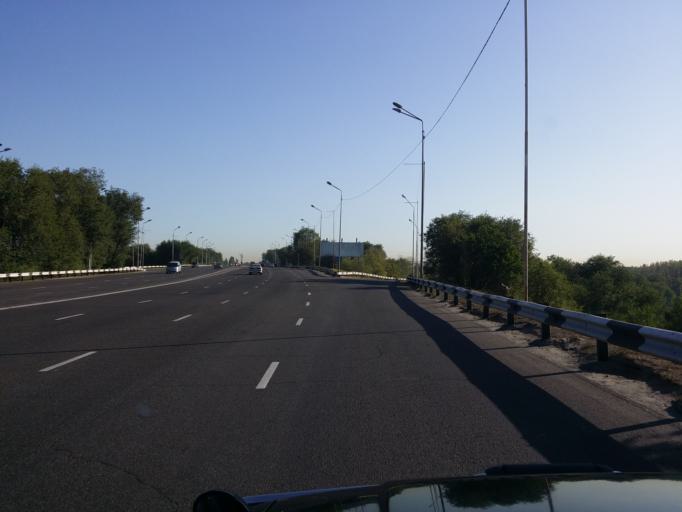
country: KZ
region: Almaty Oblysy
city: Pervomayskiy
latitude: 43.3512
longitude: 76.9375
